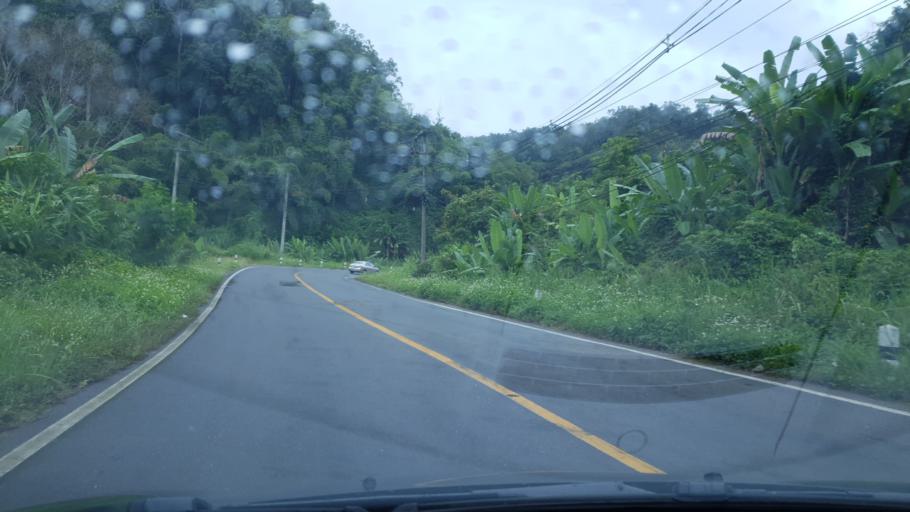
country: TH
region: Mae Hong Son
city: Mae La Noi
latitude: 18.5778
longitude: 97.9420
